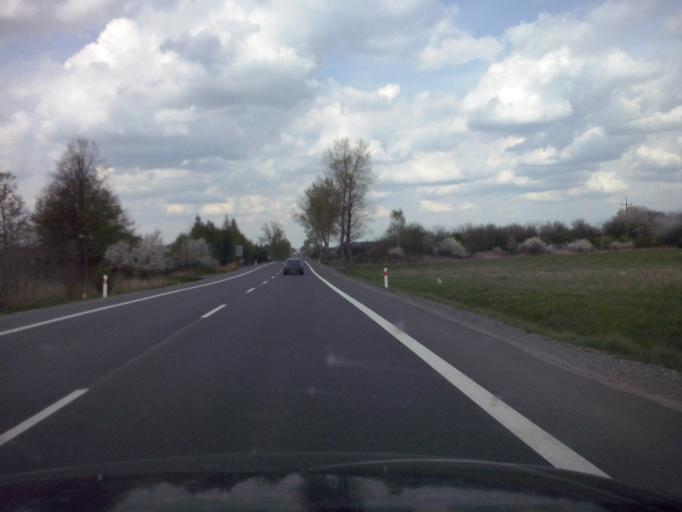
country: PL
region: Subcarpathian Voivodeship
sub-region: Powiat rzeszowski
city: Wolka Podlesna
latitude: 50.1563
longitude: 22.0792
